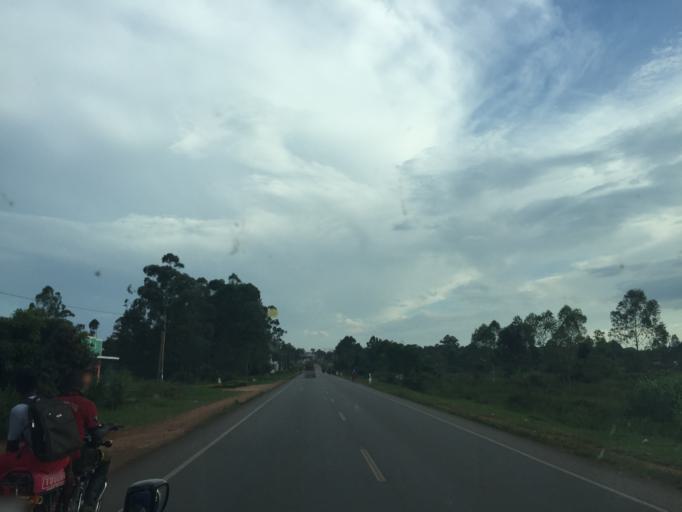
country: UG
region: Central Region
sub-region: Luwero District
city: Luwero
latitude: 0.8572
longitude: 32.4864
